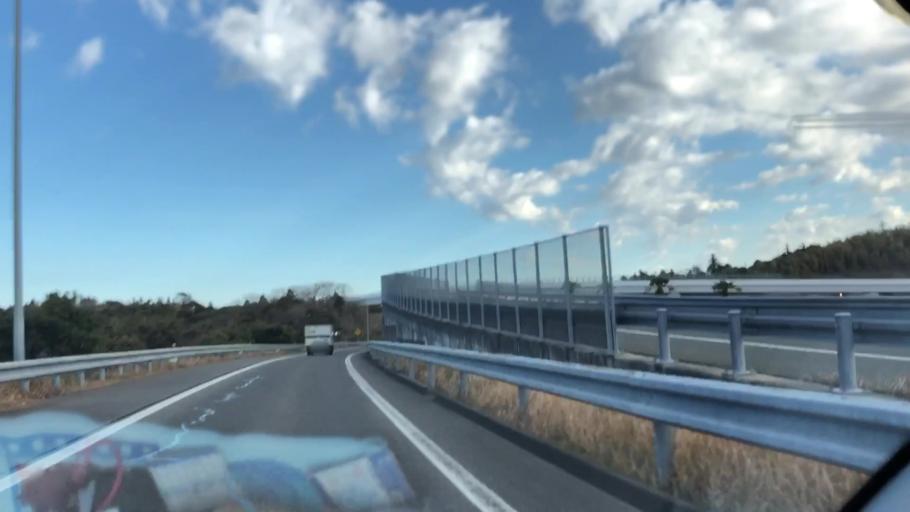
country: JP
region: Chiba
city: Kisarazu
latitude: 35.3745
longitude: 139.9768
